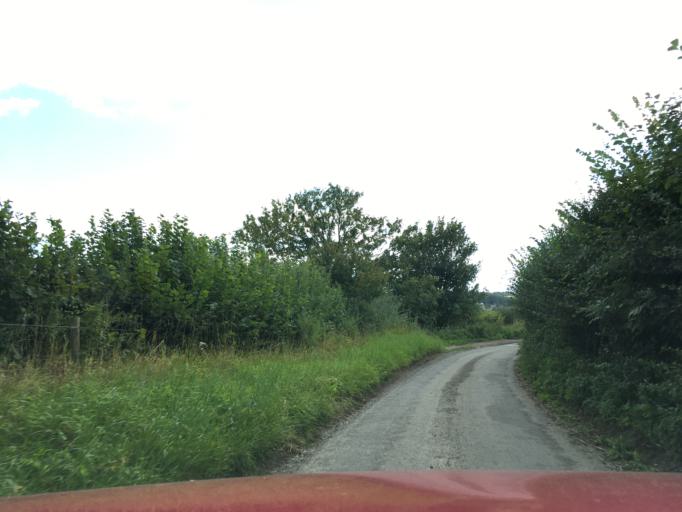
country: GB
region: England
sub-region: Wiltshire
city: Box
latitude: 51.4269
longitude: -2.2534
